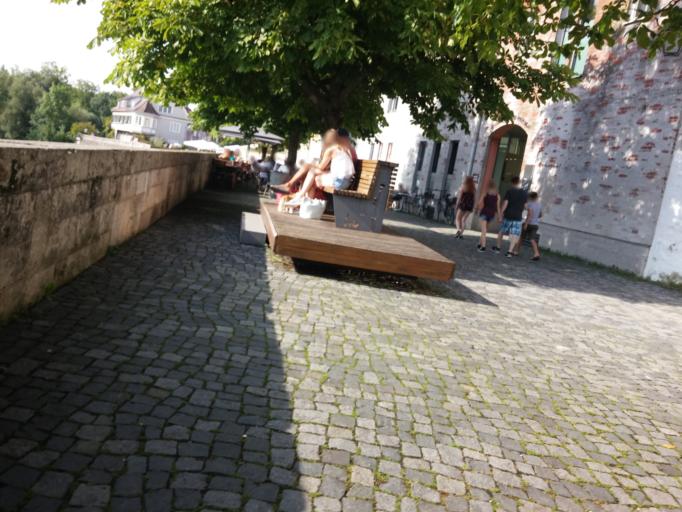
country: DE
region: Bavaria
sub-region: Upper Bavaria
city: Landsberg am Lech
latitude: 48.0485
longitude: 10.8755
